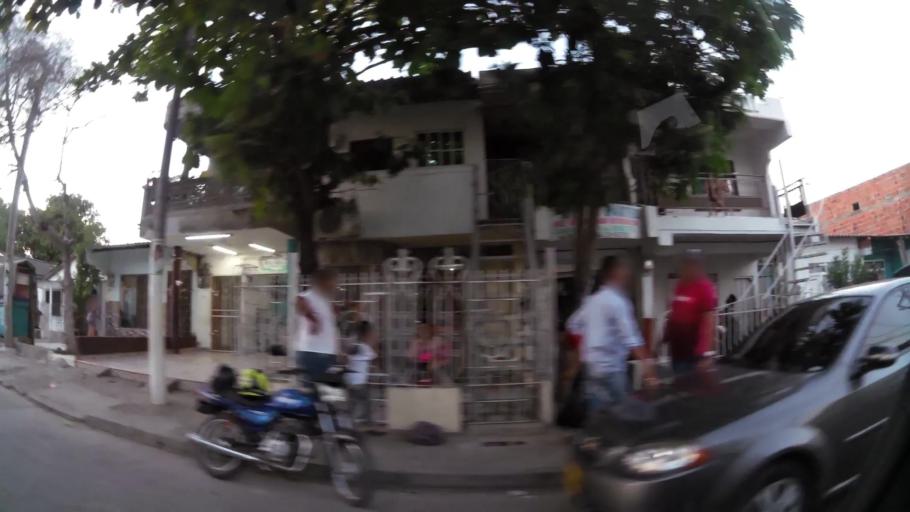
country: CO
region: Bolivar
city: Cartagena
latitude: 10.4049
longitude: -75.5168
